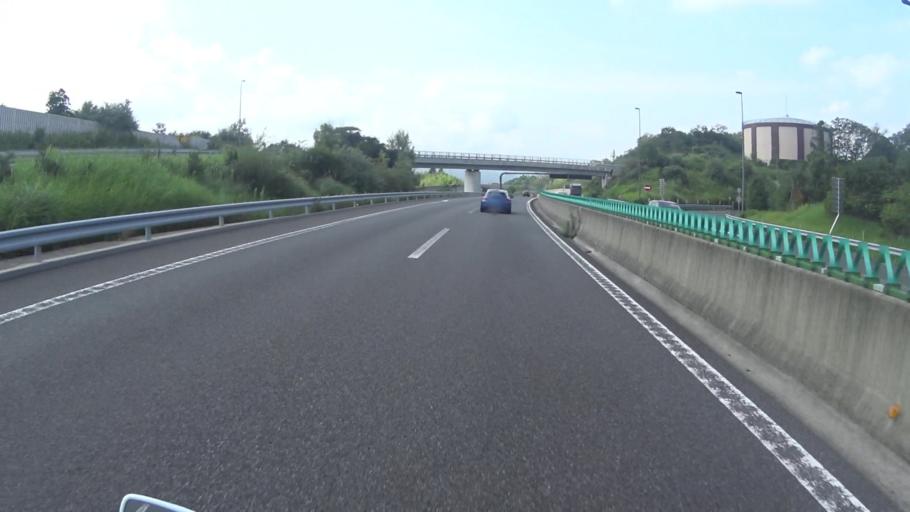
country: JP
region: Shiga Prefecture
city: Kusatsu
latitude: 34.9756
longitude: 135.9615
